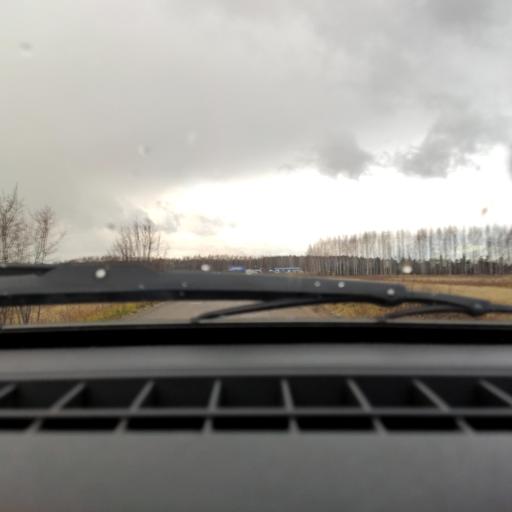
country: RU
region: Bashkortostan
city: Iglino
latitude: 54.7432
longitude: 56.3178
